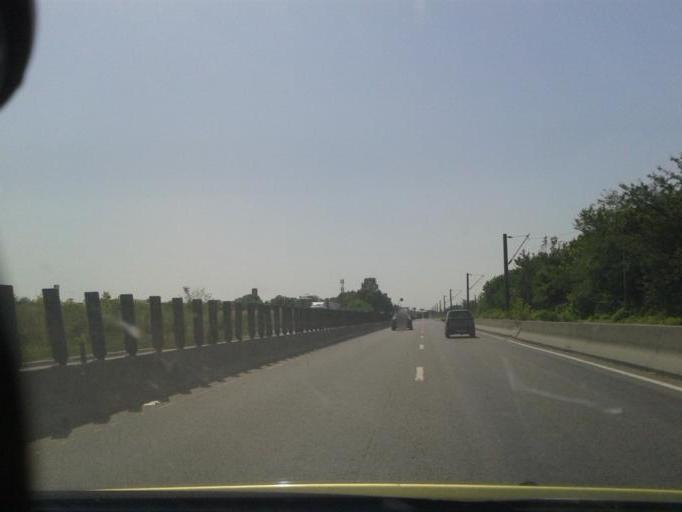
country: RO
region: Ilfov
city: Stefanestii de Jos
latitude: 44.5082
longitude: 26.1931
